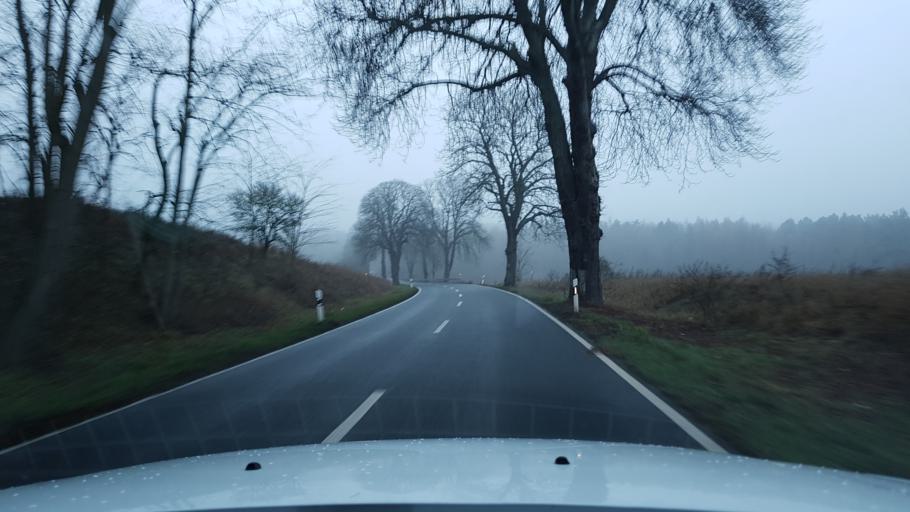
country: DE
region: Brandenburg
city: Mescherin
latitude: 53.2588
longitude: 14.4364
